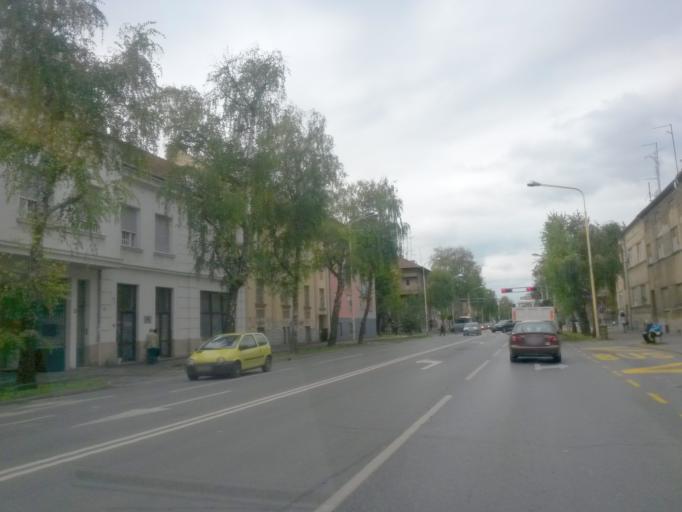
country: HR
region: Osjecko-Baranjska
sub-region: Grad Osijek
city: Osijek
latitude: 45.5562
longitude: 18.6901
